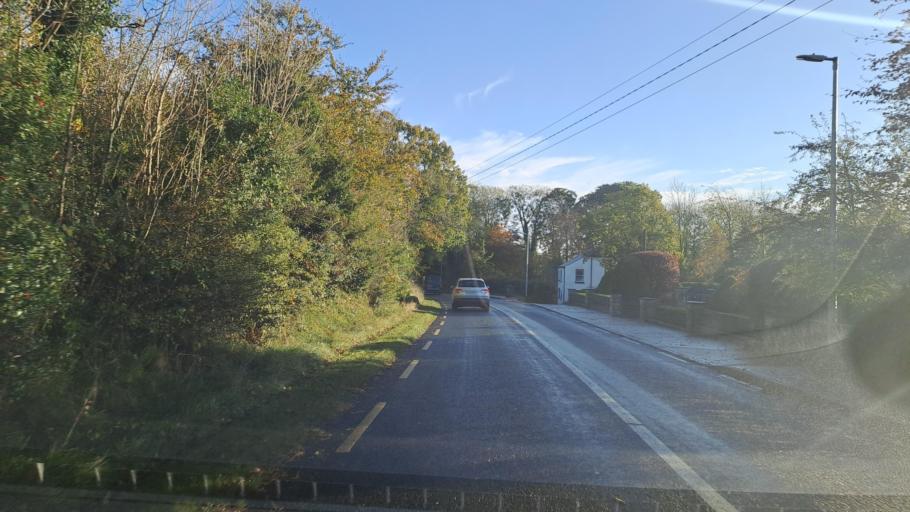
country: IE
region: Ulster
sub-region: An Cabhan
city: Cootehill
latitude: 54.1145
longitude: -7.0204
